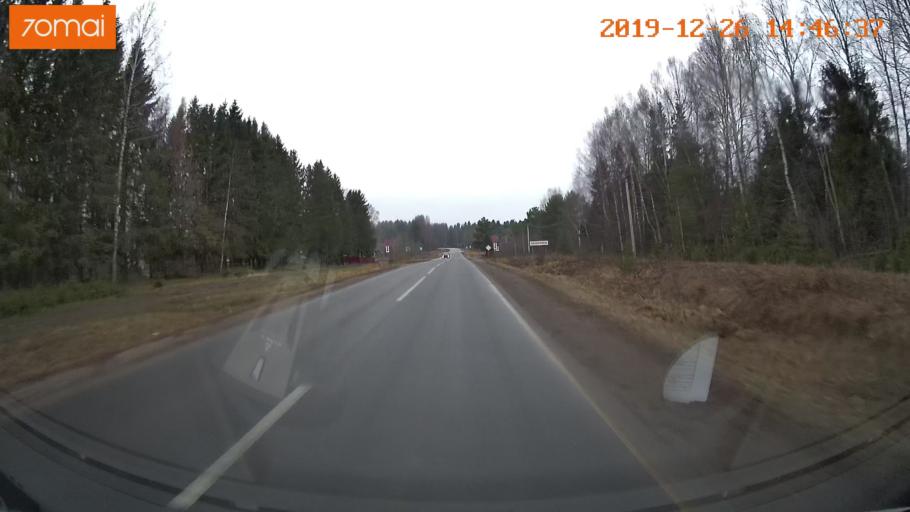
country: RU
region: Jaroslavl
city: Poshekhon'ye
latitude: 58.3378
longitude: 39.0144
